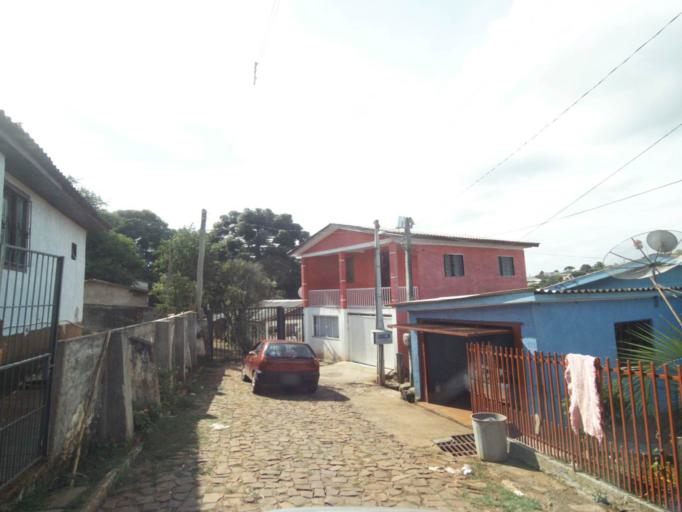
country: BR
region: Rio Grande do Sul
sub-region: Lagoa Vermelha
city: Lagoa Vermelha
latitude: -28.2070
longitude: -51.5336
